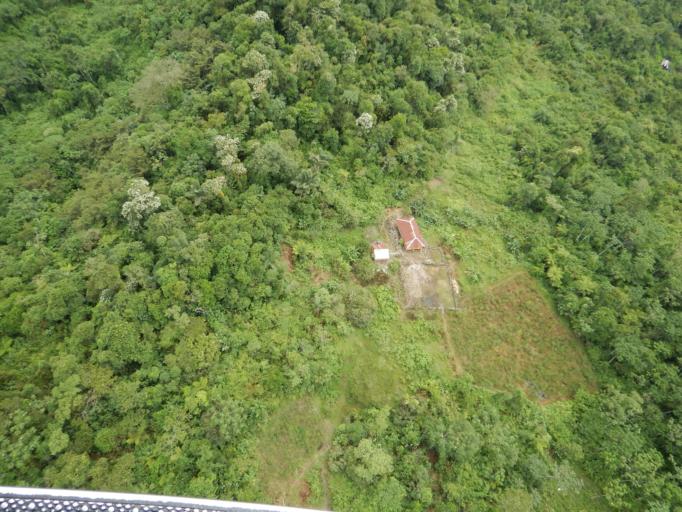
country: BO
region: Cochabamba
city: Totora
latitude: -17.3797
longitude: -65.1402
